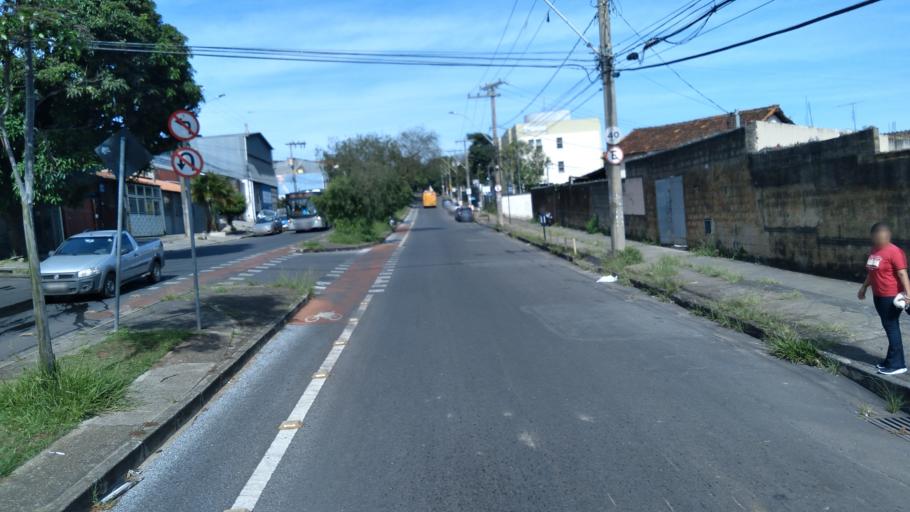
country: BR
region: Minas Gerais
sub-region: Contagem
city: Contagem
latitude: -19.8989
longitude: -44.0020
